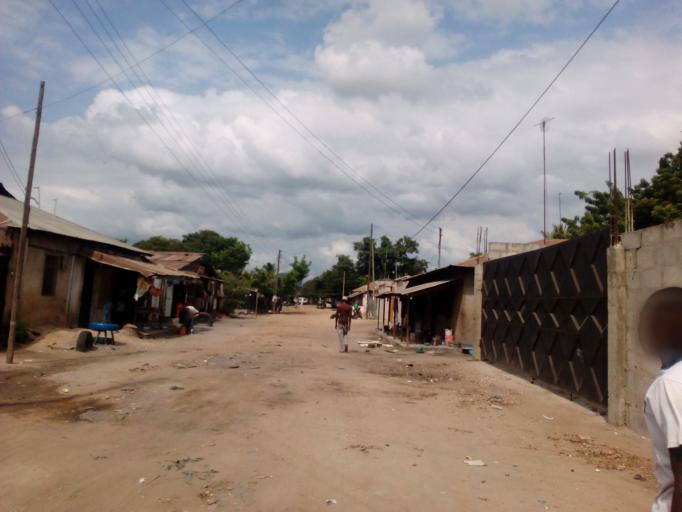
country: TZ
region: Dar es Salaam
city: Dar es Salaam
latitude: -6.8566
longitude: 39.2570
